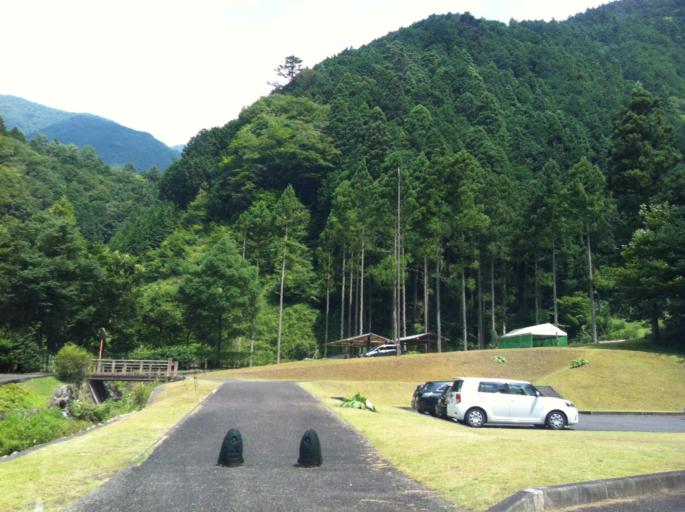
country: JP
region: Shizuoka
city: Fujinomiya
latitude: 35.2831
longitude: 138.3436
